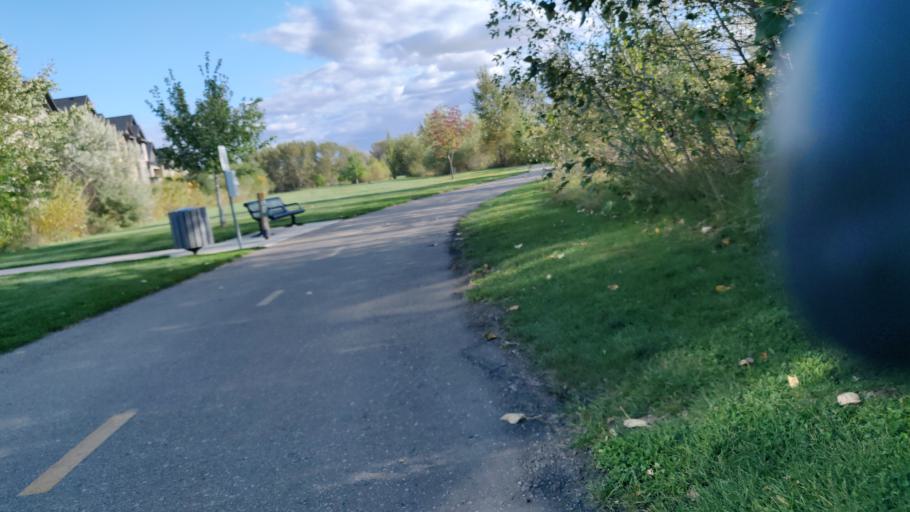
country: US
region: Idaho
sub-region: Ada County
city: Boise
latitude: 43.5741
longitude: -116.1453
